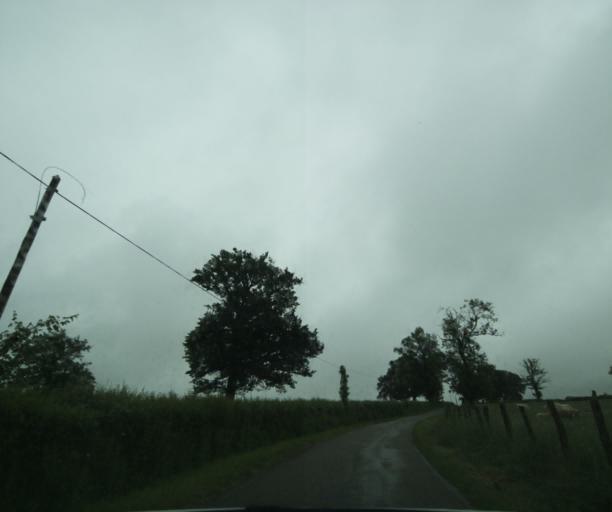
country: FR
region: Bourgogne
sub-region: Departement de Saone-et-Loire
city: Palinges
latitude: 46.4739
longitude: 4.2134
